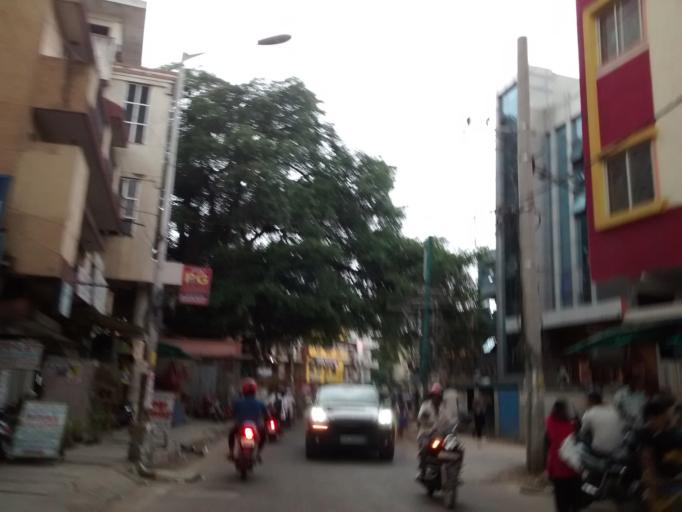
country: IN
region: Karnataka
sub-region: Bangalore Urban
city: Bangalore
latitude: 12.9218
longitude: 77.6108
